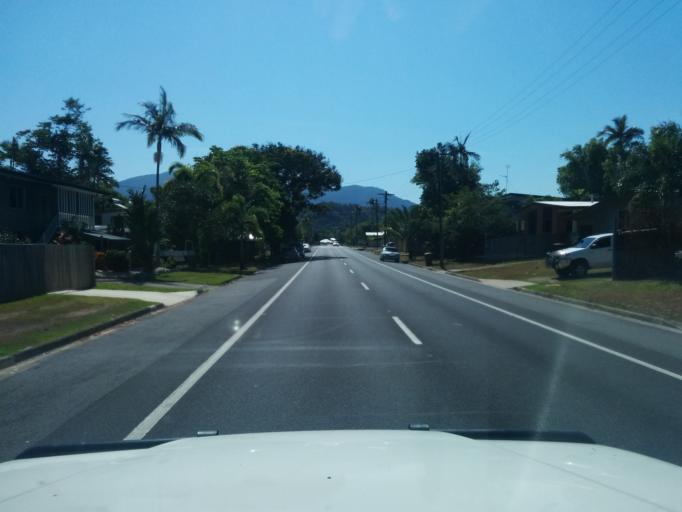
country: AU
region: Queensland
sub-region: Cairns
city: Cairns
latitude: -16.9027
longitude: 145.7376
